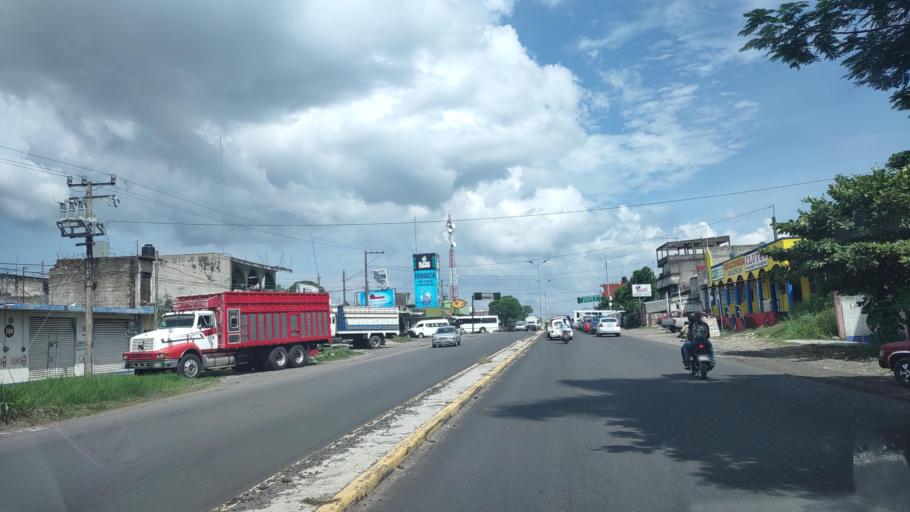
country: MX
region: Veracruz
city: Martinez de la Torre
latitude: 20.0727
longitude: -97.0656
